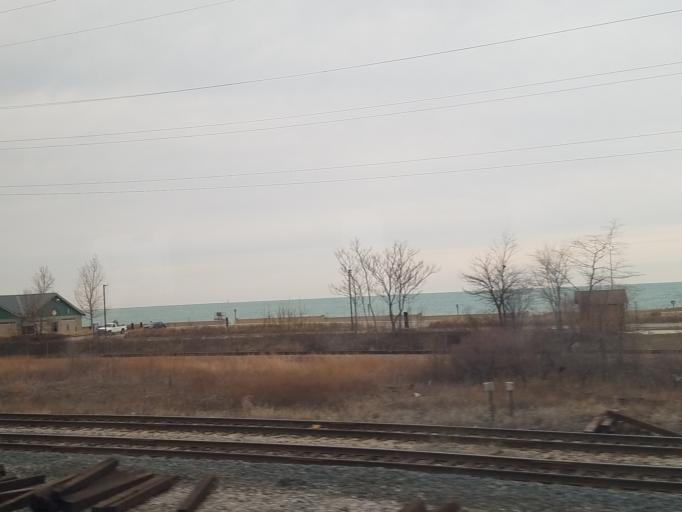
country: US
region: Indiana
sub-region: Lake County
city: Whiting
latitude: 41.6844
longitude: -87.4912
